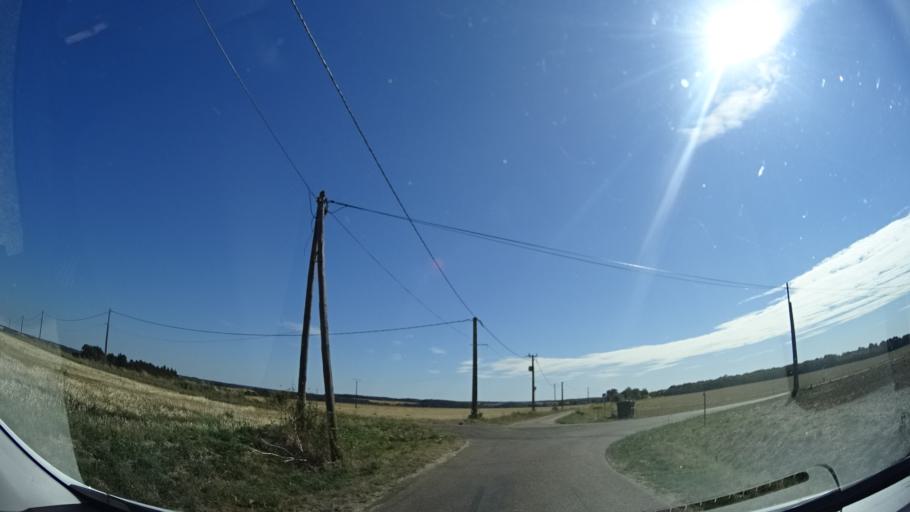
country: FR
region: Centre
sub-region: Departement du Loiret
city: Trigueres
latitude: 47.9474
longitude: 2.9618
